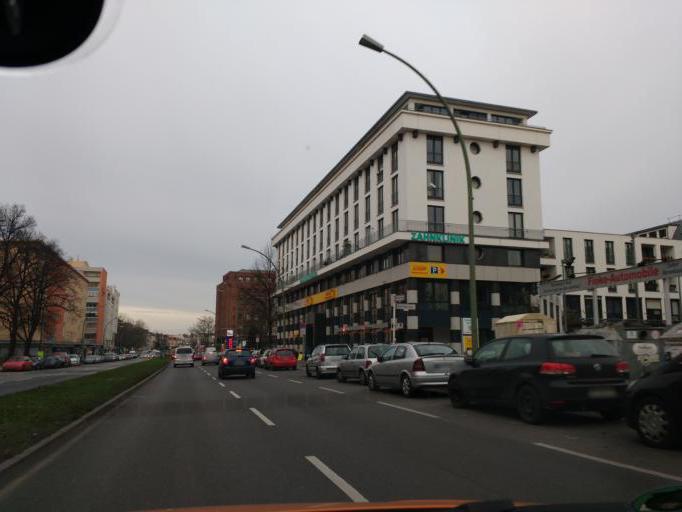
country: DE
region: Berlin
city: Mariendorf
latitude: 52.4506
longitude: 13.3849
